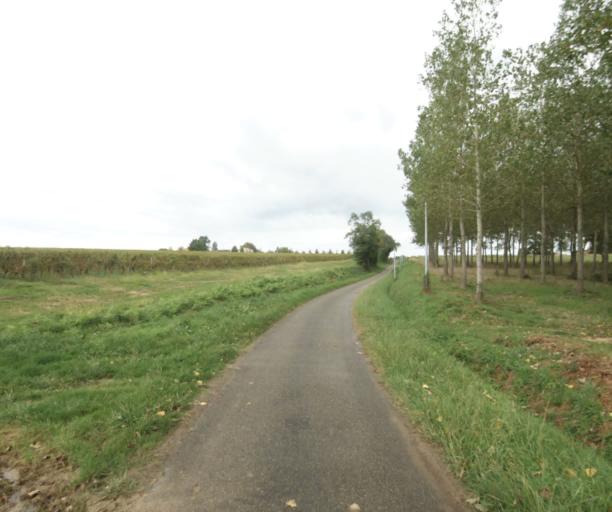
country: FR
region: Midi-Pyrenees
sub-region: Departement du Gers
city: Cazaubon
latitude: 43.8892
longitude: -0.1065
